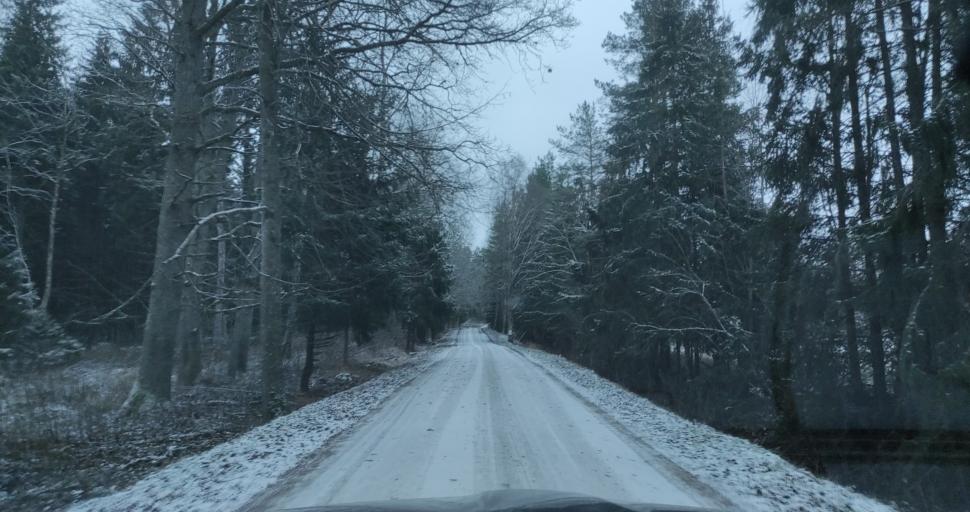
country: LV
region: Kuldigas Rajons
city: Kuldiga
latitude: 56.9791
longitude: 22.0302
